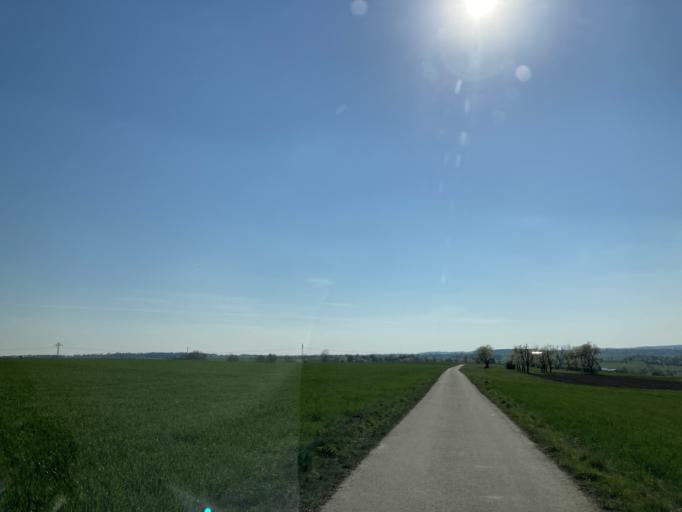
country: DE
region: Baden-Wuerttemberg
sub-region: Regierungsbezirk Stuttgart
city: Herrenberg
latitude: 48.5551
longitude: 8.9291
